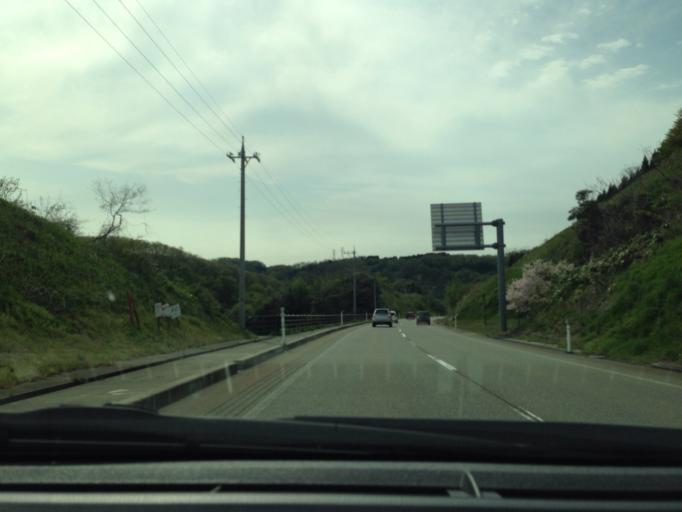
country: JP
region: Ishikawa
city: Tsubata
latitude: 36.5489
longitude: 136.7398
